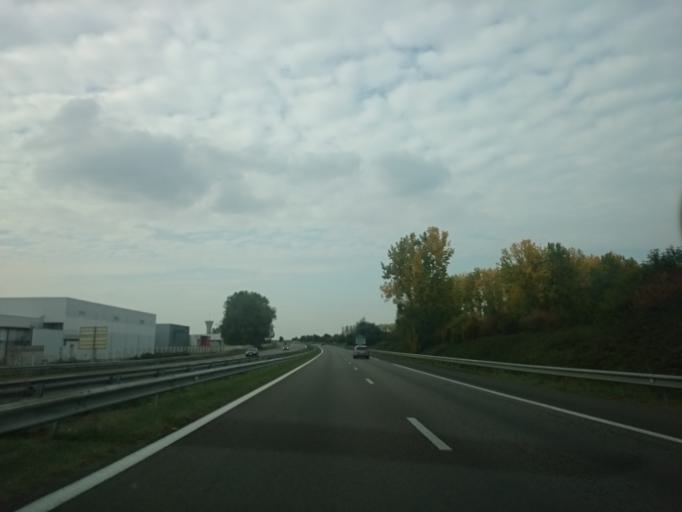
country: FR
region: Brittany
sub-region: Departement d'Ille-et-Vilaine
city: Pleumeleuc
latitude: 48.1798
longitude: -1.9282
